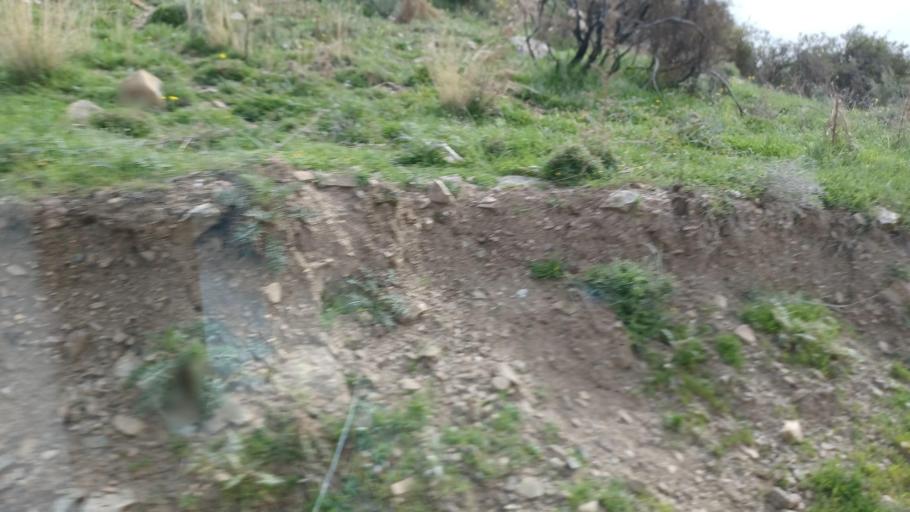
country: CY
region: Pafos
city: Pegeia
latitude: 34.9488
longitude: 32.3554
